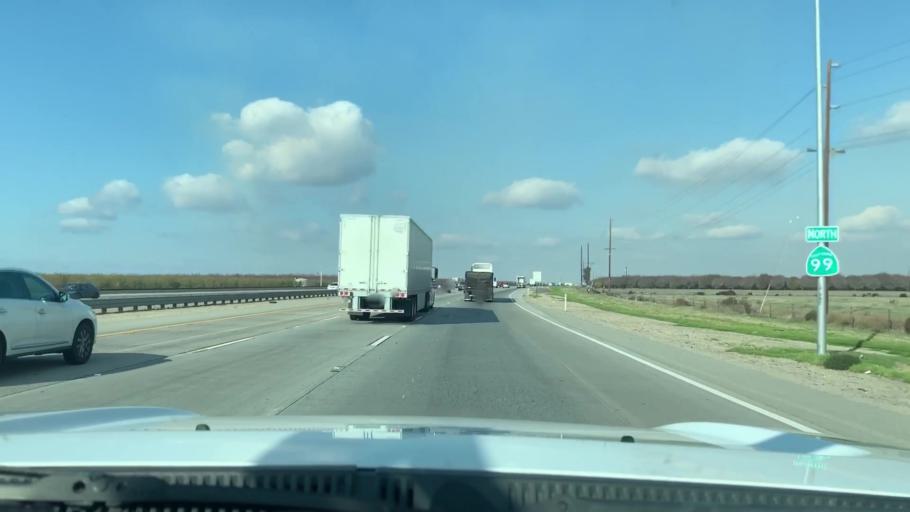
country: US
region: California
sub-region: Kern County
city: Shafter
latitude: 35.5337
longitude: -119.1916
